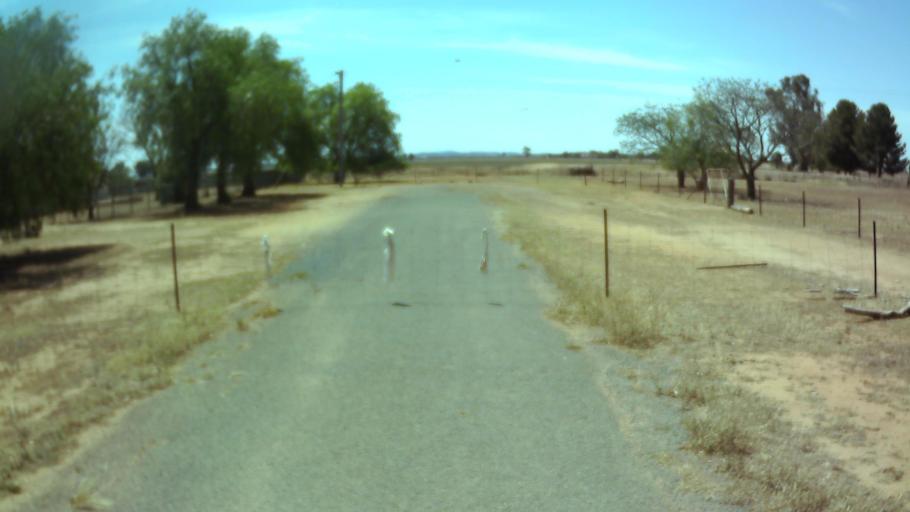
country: AU
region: New South Wales
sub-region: Weddin
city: Grenfell
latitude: -33.8402
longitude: 147.7397
